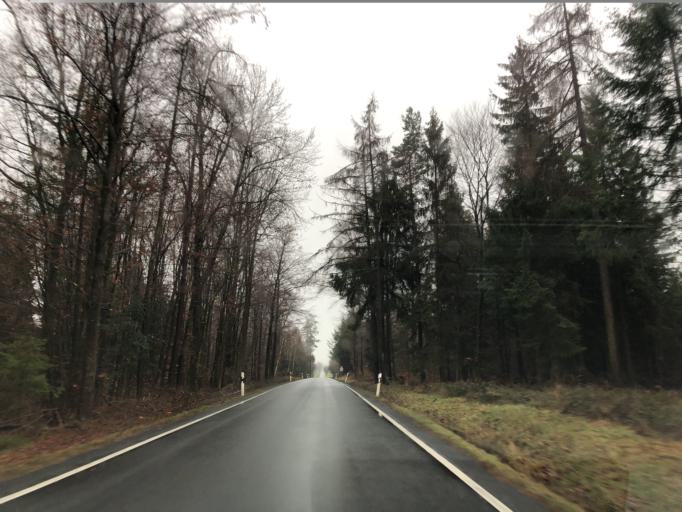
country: DE
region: Hesse
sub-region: Regierungsbezirk Darmstadt
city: Lutzelbach
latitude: 49.7282
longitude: 9.0849
